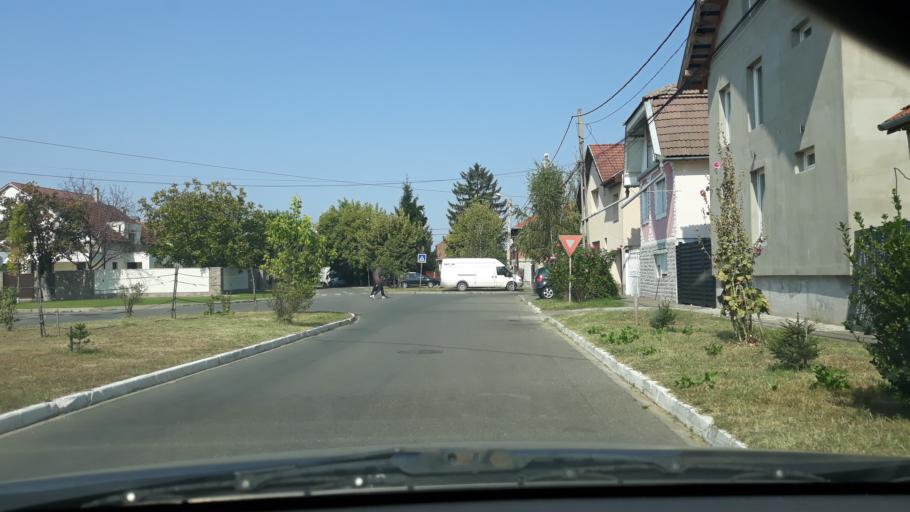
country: RO
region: Bihor
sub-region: Comuna Biharea
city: Oradea
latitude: 47.0423
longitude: 21.9511
